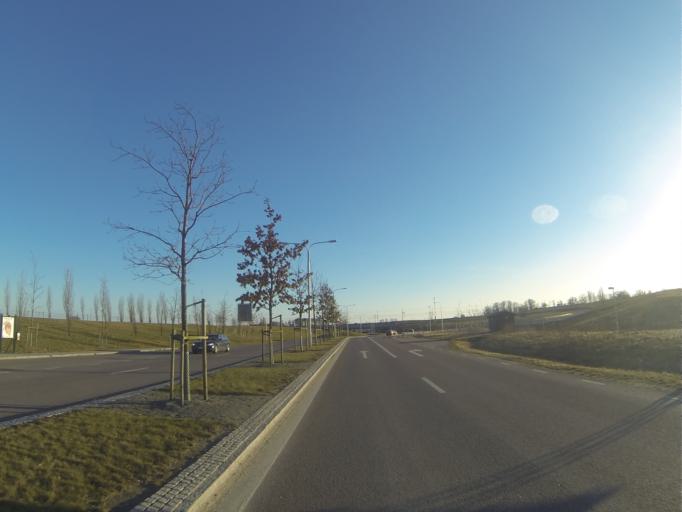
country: SE
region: Skane
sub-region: Malmo
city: Bunkeflostrand
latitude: 55.5494
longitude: 12.9826
